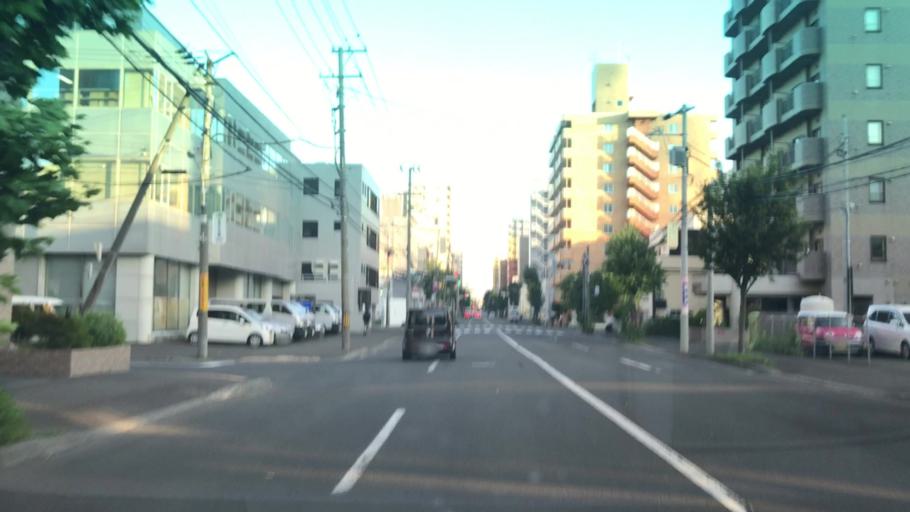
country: JP
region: Hokkaido
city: Sapporo
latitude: 43.0668
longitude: 141.3360
